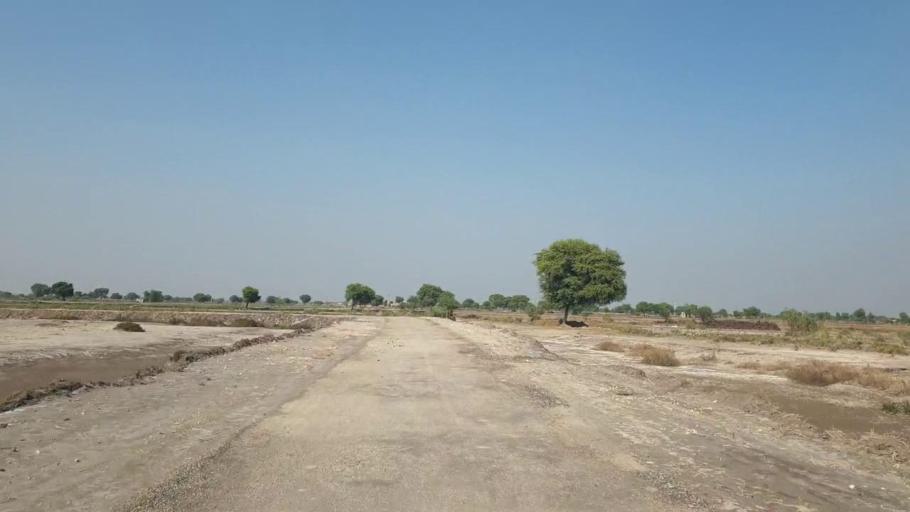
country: PK
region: Sindh
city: Sehwan
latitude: 26.4274
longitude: 67.8333
